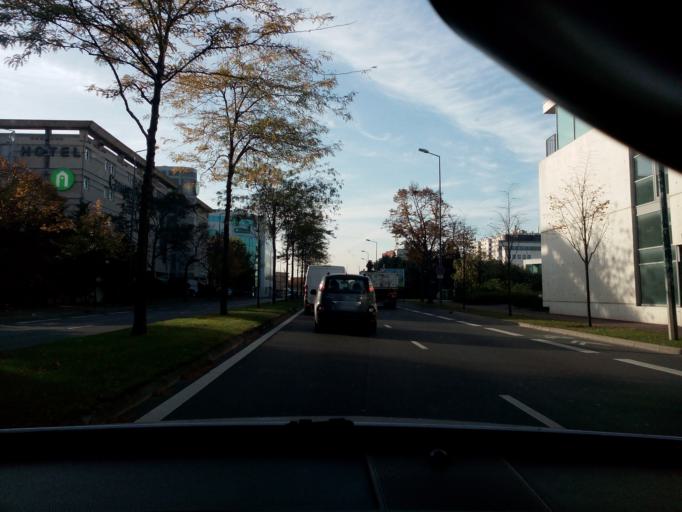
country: FR
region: Ile-de-France
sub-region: Departement des Hauts-de-Seine
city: Gennevilliers
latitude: 48.9357
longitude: 2.3036
